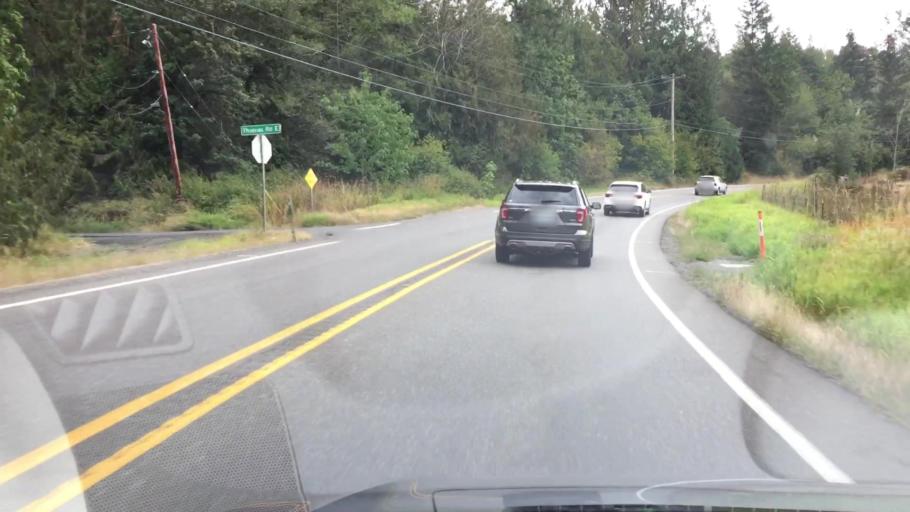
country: US
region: Washington
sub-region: Pierce County
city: Eatonville
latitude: 46.9404
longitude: -122.2807
